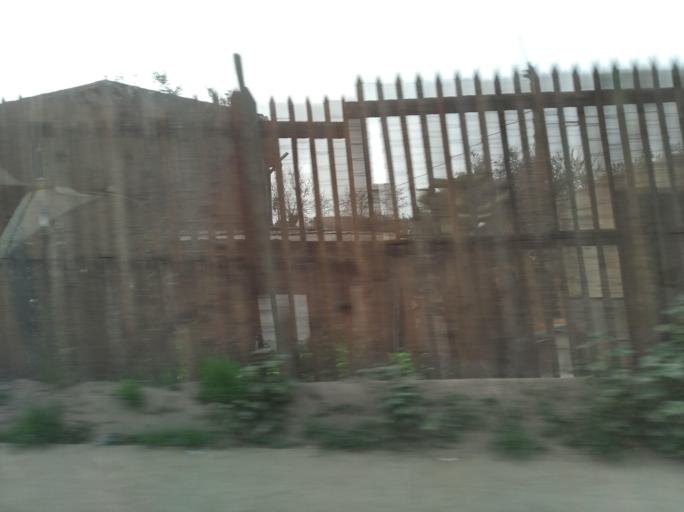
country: CL
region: Santiago Metropolitan
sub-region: Provincia de Chacabuco
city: Lampa
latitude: -33.2846
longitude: -70.8875
